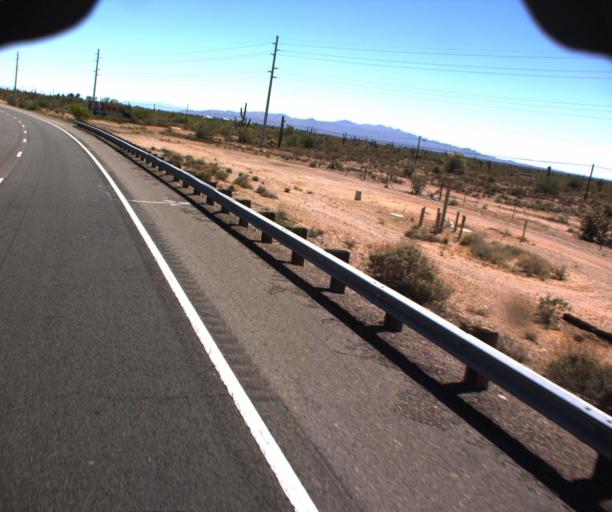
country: US
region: Arizona
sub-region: Maricopa County
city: Wickenburg
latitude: 33.8410
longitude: -112.6125
